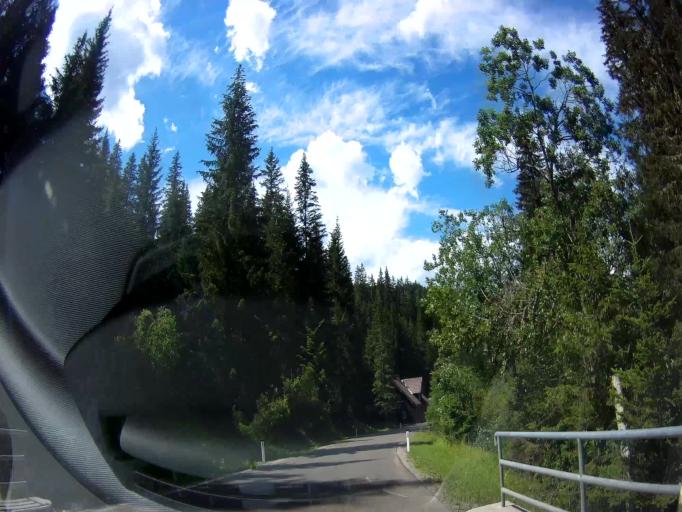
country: AT
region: Styria
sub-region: Politischer Bezirk Murau
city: Stadl an der Mur
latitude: 47.0165
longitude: 14.0048
